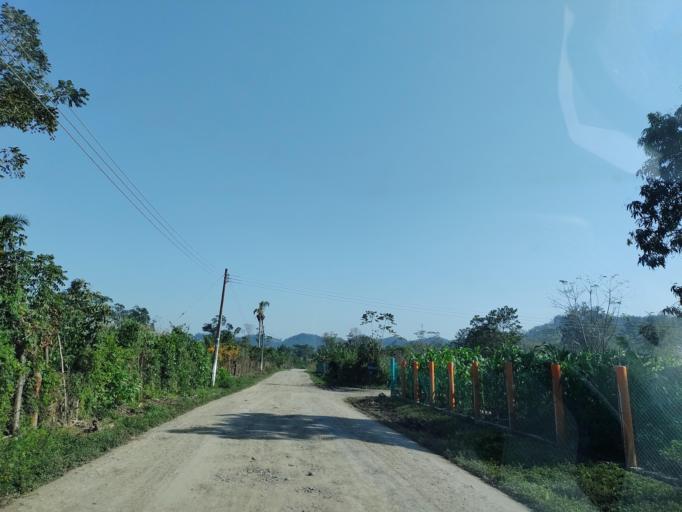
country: MX
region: Veracruz
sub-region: Papantla
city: Polutla
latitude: 20.5160
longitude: -97.2470
